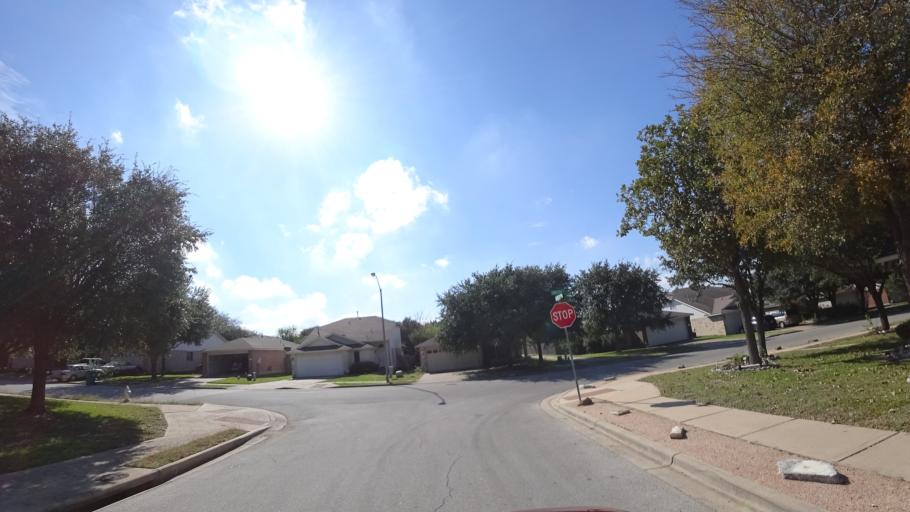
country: US
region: Texas
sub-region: Travis County
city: Windemere
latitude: 30.4460
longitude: -97.6567
